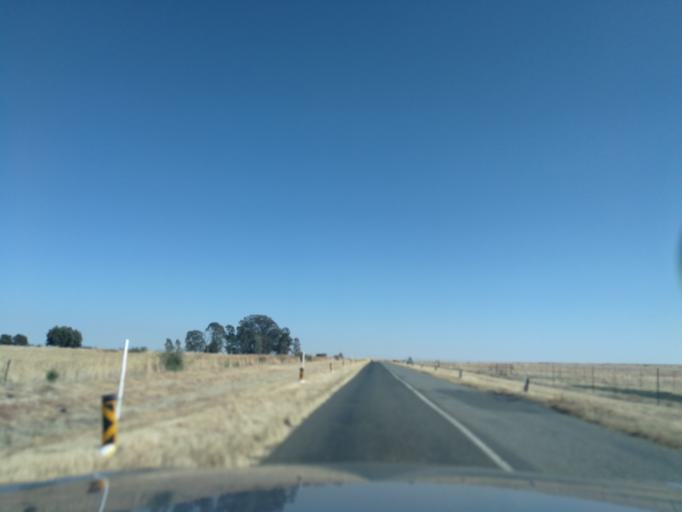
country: ZA
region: Orange Free State
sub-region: Fezile Dabi District Municipality
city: Kroonstad
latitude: -27.8824
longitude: 27.4622
